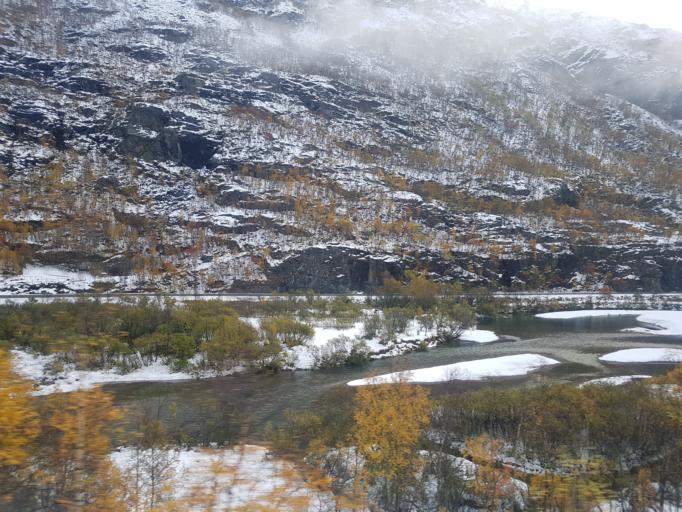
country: NO
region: Sor-Trondelag
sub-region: Oppdal
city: Oppdal
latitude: 62.3585
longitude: 9.6315
